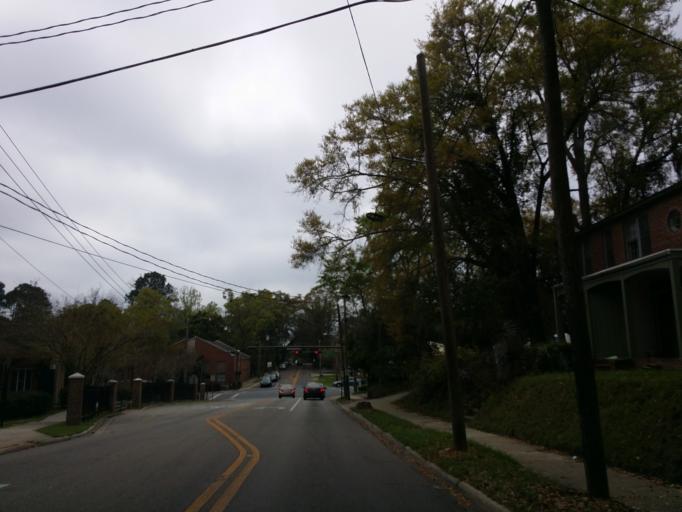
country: US
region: Florida
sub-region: Leon County
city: Tallahassee
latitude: 30.4456
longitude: -84.2771
